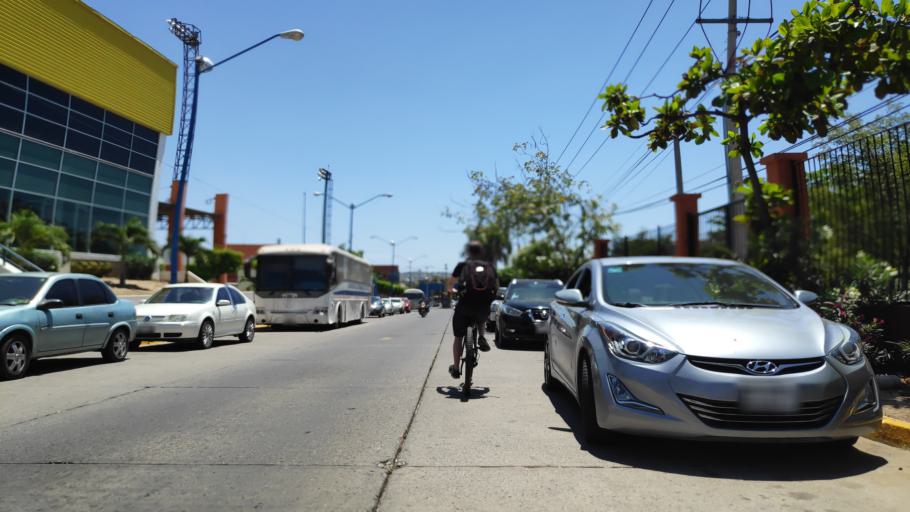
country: MX
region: Sinaloa
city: Culiacan
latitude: 24.8238
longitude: -107.3835
